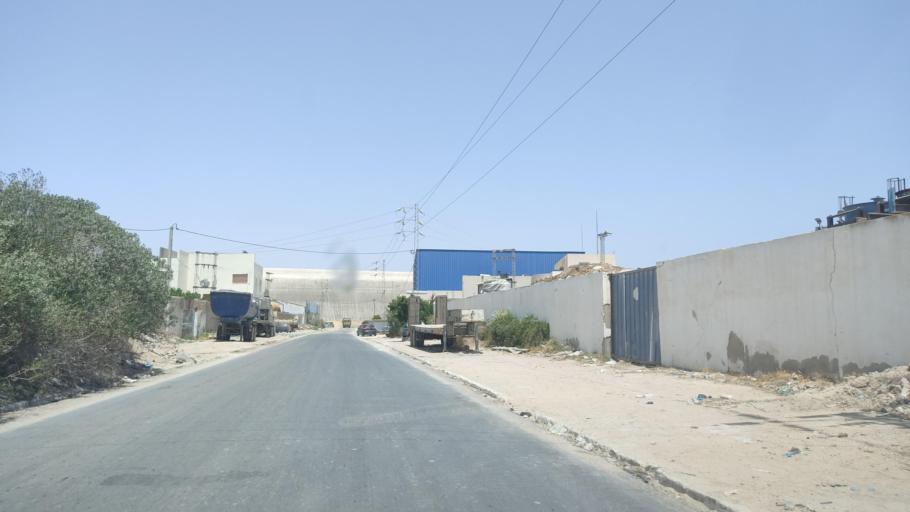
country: TN
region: Safaqis
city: Sfax
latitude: 34.6904
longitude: 10.7261
